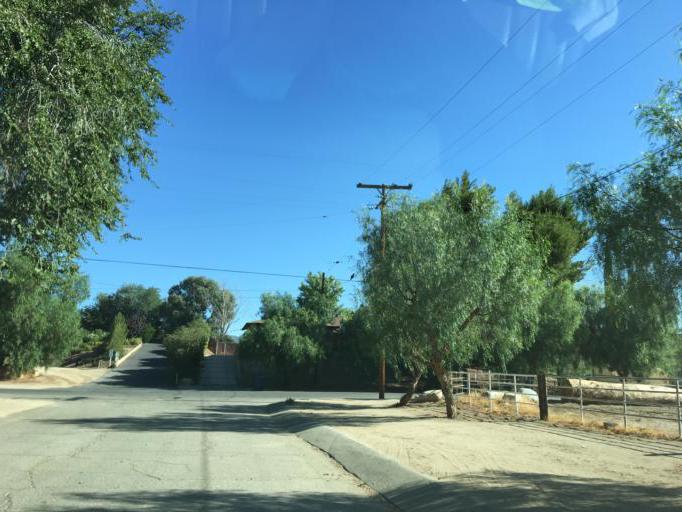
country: US
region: California
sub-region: Los Angeles County
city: Acton
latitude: 34.4677
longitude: -118.1984
